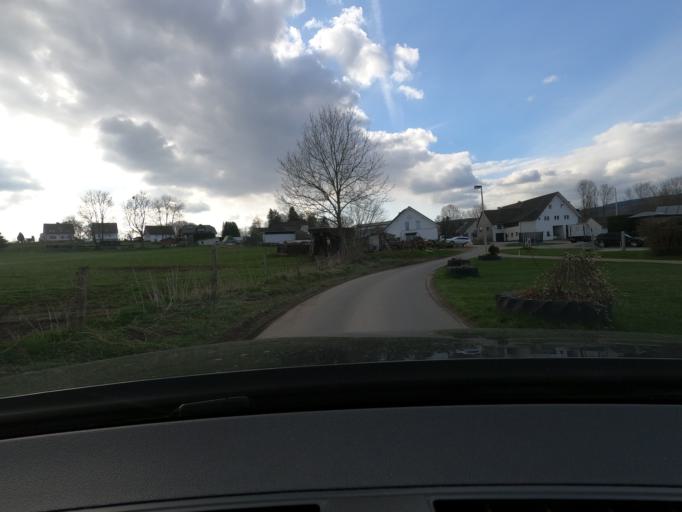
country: DE
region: North Rhine-Westphalia
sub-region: Regierungsbezirk Arnsberg
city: Herscheid
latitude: 51.1145
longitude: 7.7794
